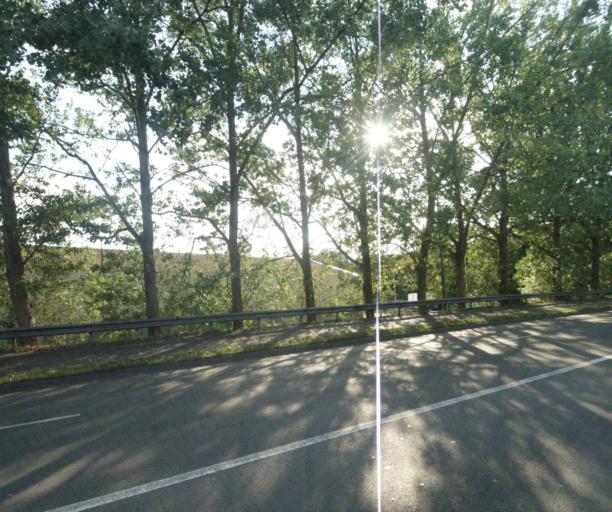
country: FR
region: Nord-Pas-de-Calais
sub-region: Departement du Nord
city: Ronchin
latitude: 50.6223
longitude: 3.0851
